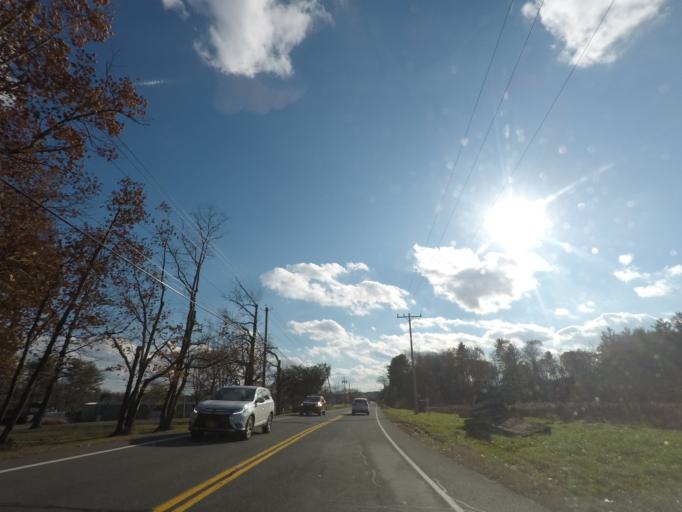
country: US
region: New York
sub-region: Schenectady County
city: Niskayuna
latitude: 42.8146
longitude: -73.8657
